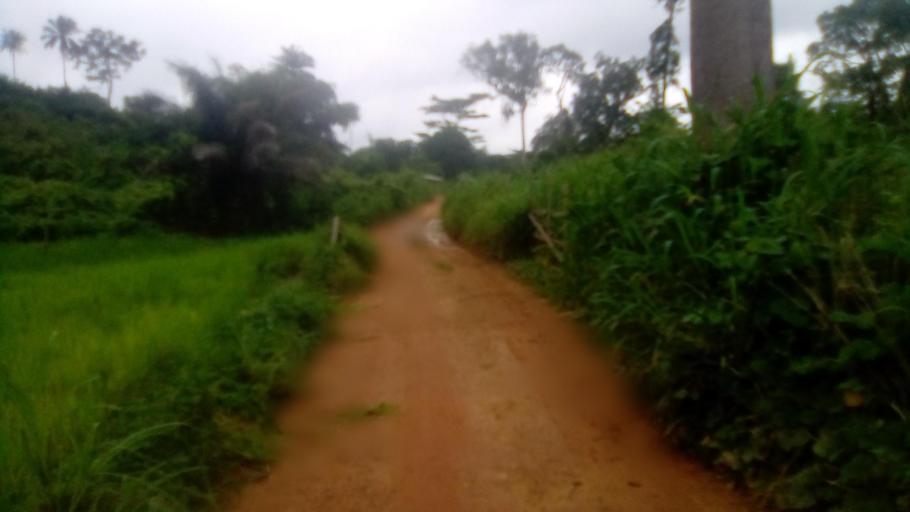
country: SL
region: Eastern Province
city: Kailahun
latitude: 8.3084
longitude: -10.5603
